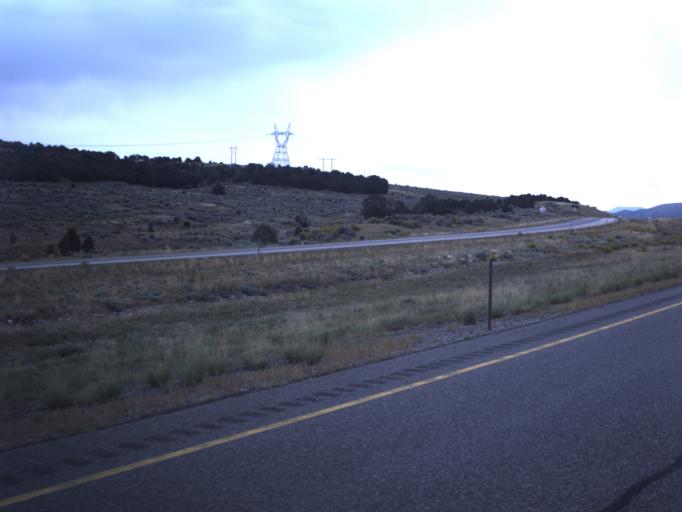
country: US
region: Utah
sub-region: Sevier County
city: Monroe
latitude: 38.5542
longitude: -112.4219
